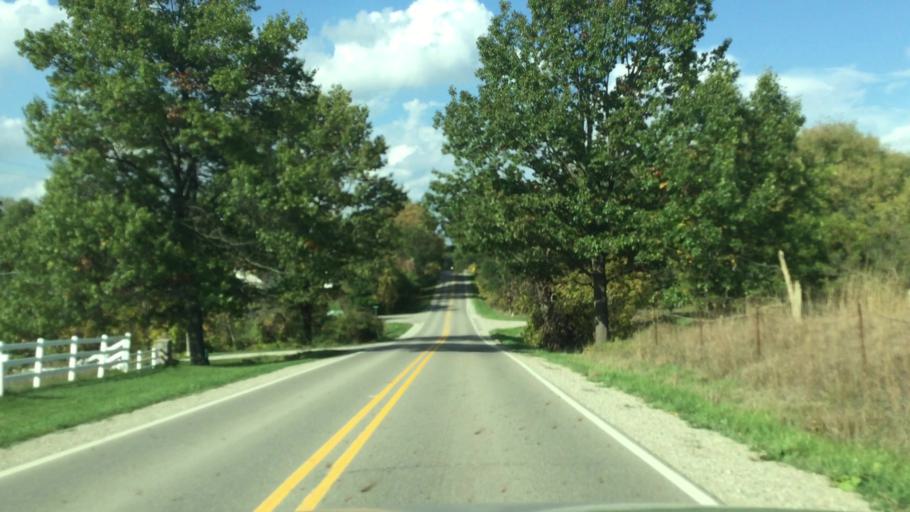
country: US
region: Michigan
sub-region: Oakland County
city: Milford
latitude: 42.6591
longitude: -83.7009
